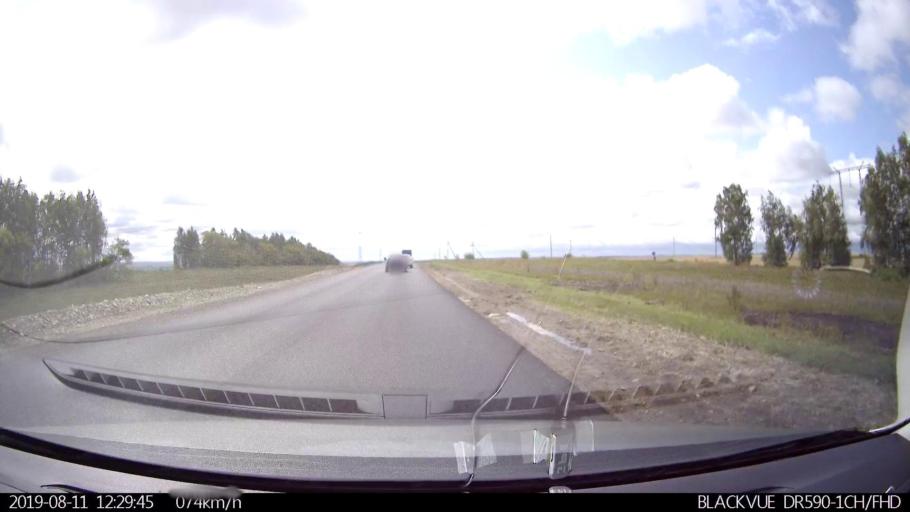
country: RU
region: Ulyanovsk
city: Ignatovka
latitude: 53.8318
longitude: 47.8996
